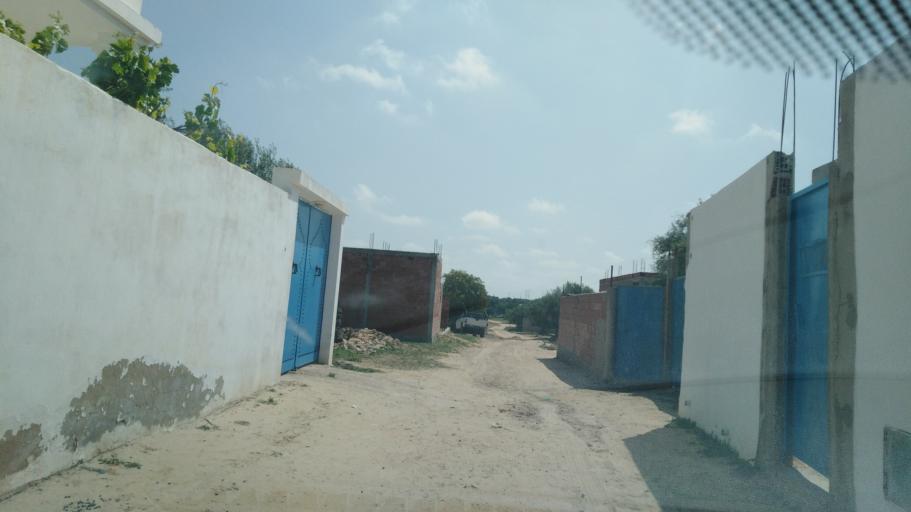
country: TN
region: Safaqis
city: Sfax
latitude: 34.7293
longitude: 10.5643
